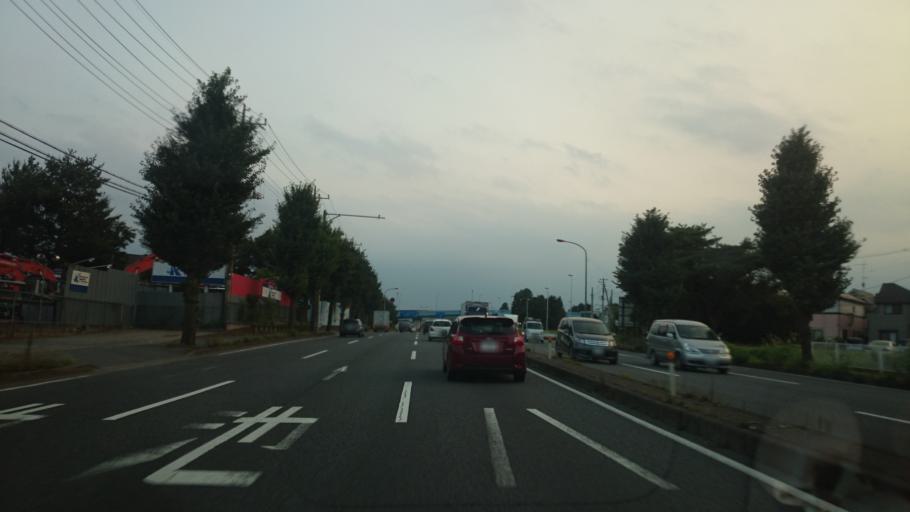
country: JP
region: Saitama
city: Ageoshimo
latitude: 35.9318
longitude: 139.5953
